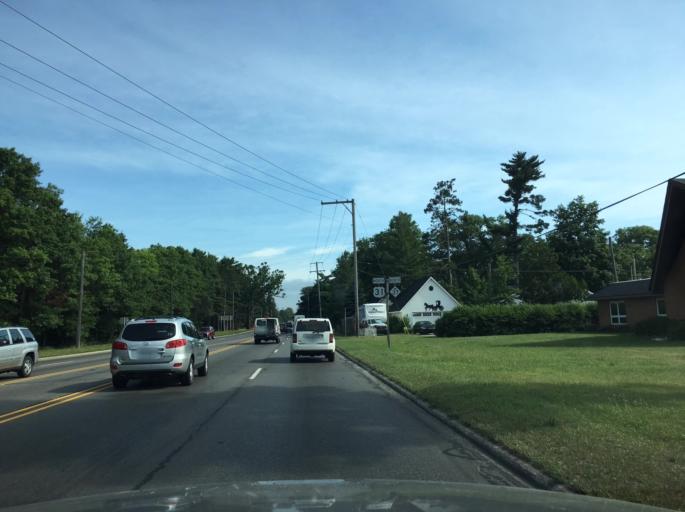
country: US
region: Michigan
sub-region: Grand Traverse County
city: Traverse City
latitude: 44.7523
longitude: -85.6350
